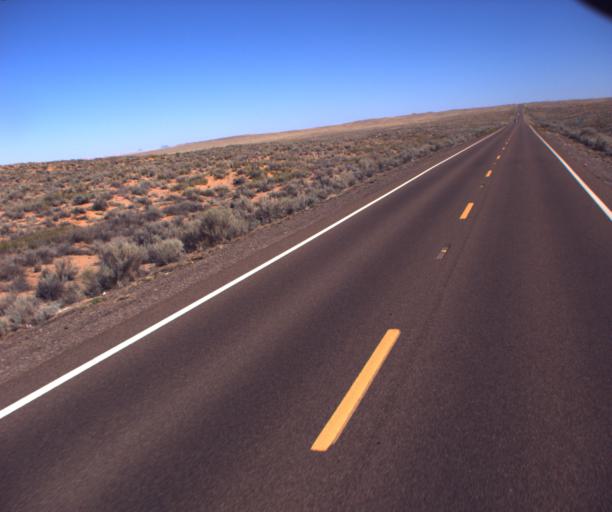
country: US
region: Arizona
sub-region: Navajo County
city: Winslow
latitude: 35.0426
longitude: -110.6071
